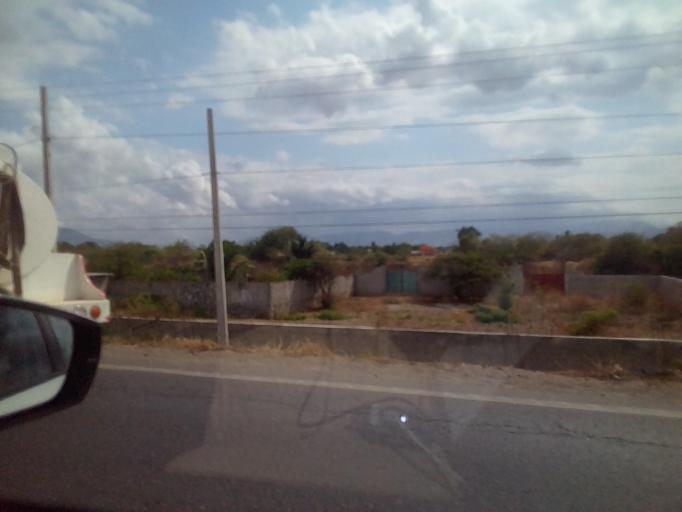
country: MX
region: Oaxaca
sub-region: Santo Domingo Tehuantepec
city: Santo Domingo Tehuantepec
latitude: 16.3086
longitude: -95.2356
